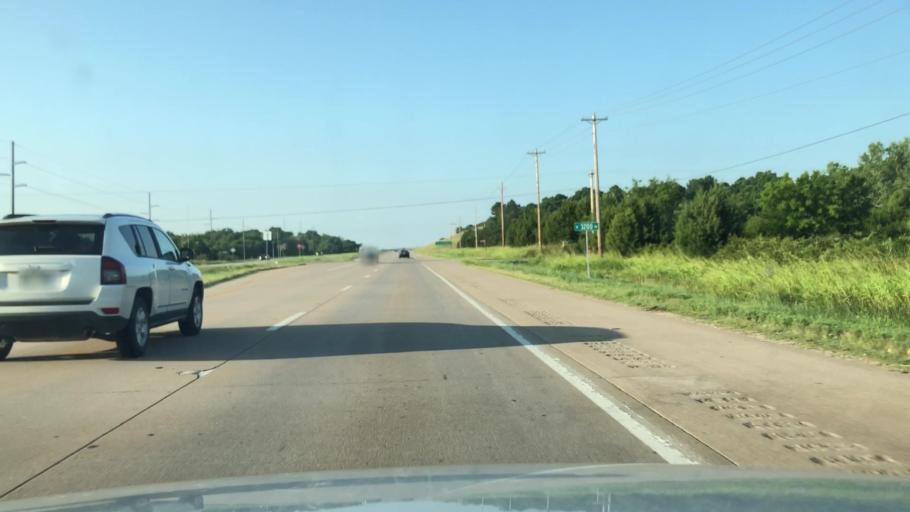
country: US
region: Oklahoma
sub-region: Washington County
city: Bartlesville
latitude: 36.5549
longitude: -95.9287
